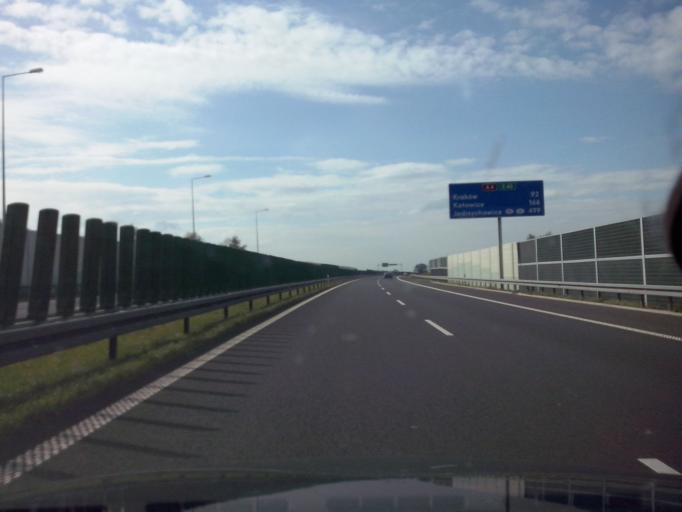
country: PL
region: Lesser Poland Voivodeship
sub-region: Powiat tarnowski
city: Tarnow
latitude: 50.0548
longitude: 21.0065
